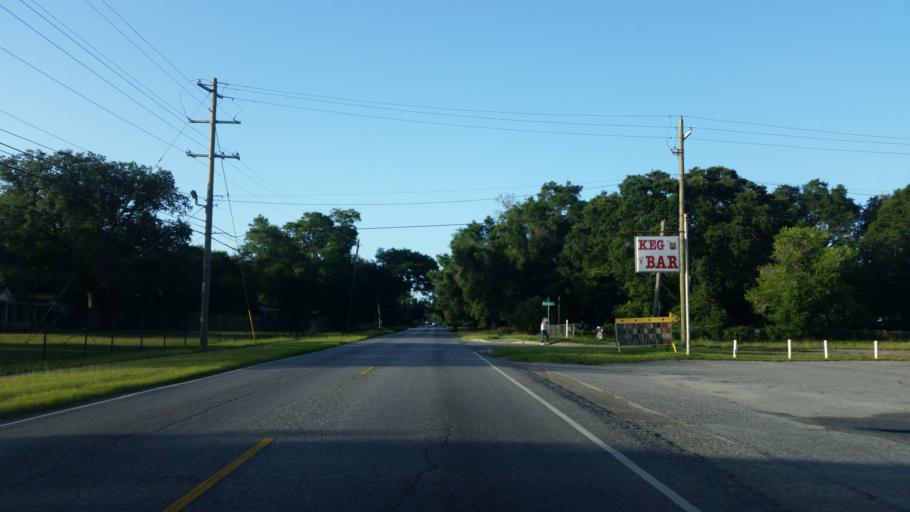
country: US
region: Florida
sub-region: Escambia County
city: Warrington
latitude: 30.3946
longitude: -87.2733
